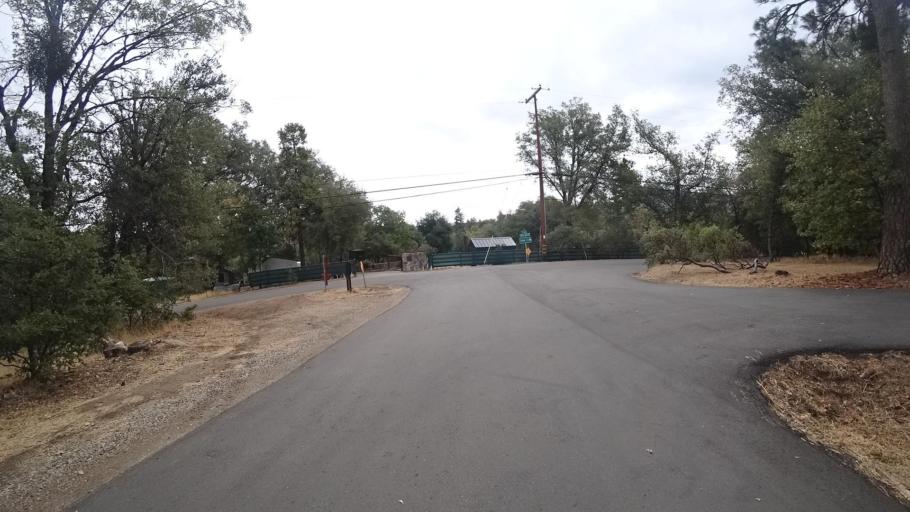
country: US
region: California
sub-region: San Diego County
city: Julian
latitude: 33.0505
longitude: -116.6240
